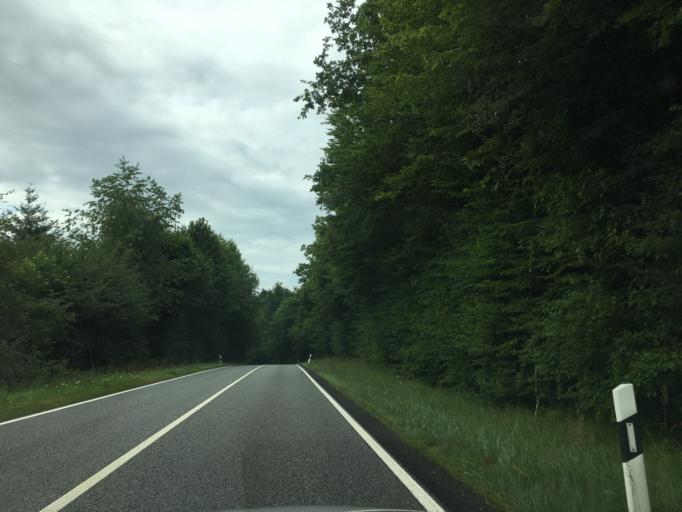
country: DE
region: Hesse
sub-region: Regierungsbezirk Darmstadt
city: Birstein
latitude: 50.3300
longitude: 9.2882
